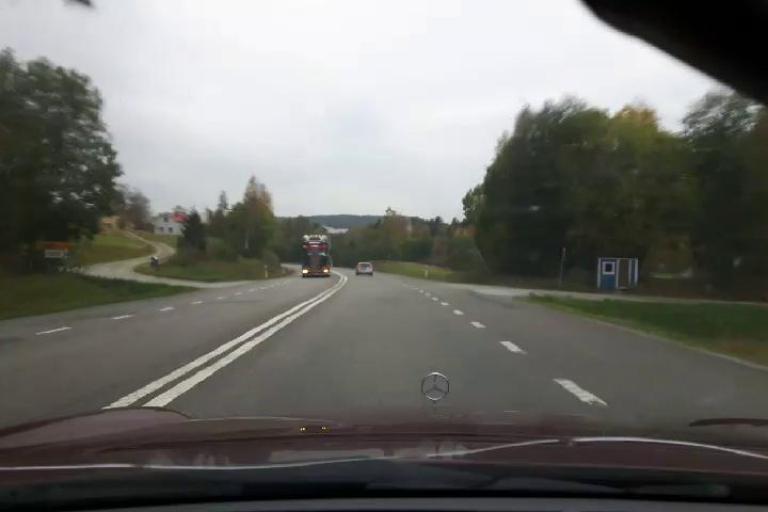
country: SE
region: Vaesternorrland
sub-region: Kramfors Kommun
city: Nordingra
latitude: 63.0228
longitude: 18.2970
